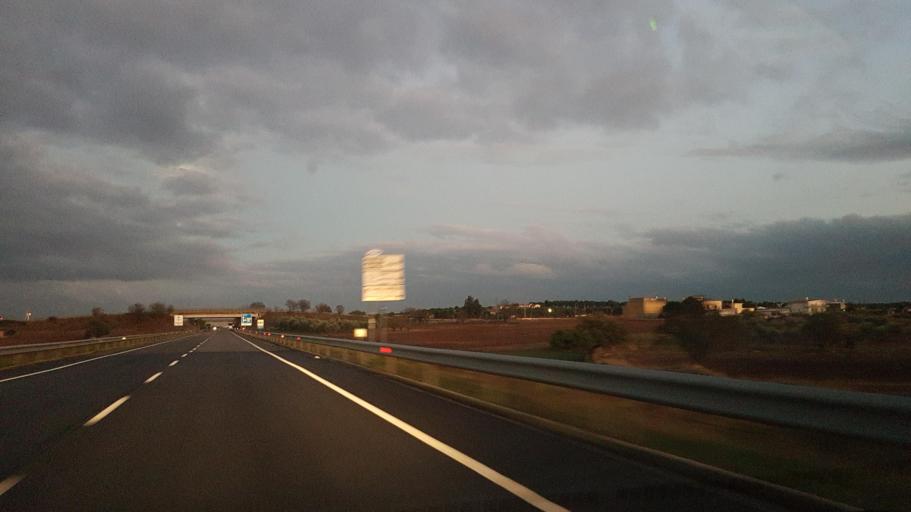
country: IT
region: Apulia
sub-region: Provincia di Taranto
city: Laterza
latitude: 40.6496
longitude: 16.8160
